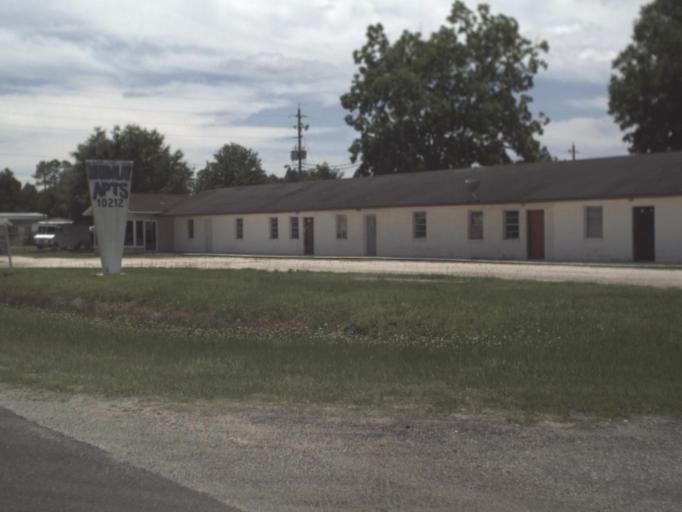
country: US
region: Florida
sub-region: Nassau County
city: Nassau Village-Ratliff
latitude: 30.4213
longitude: -81.7532
